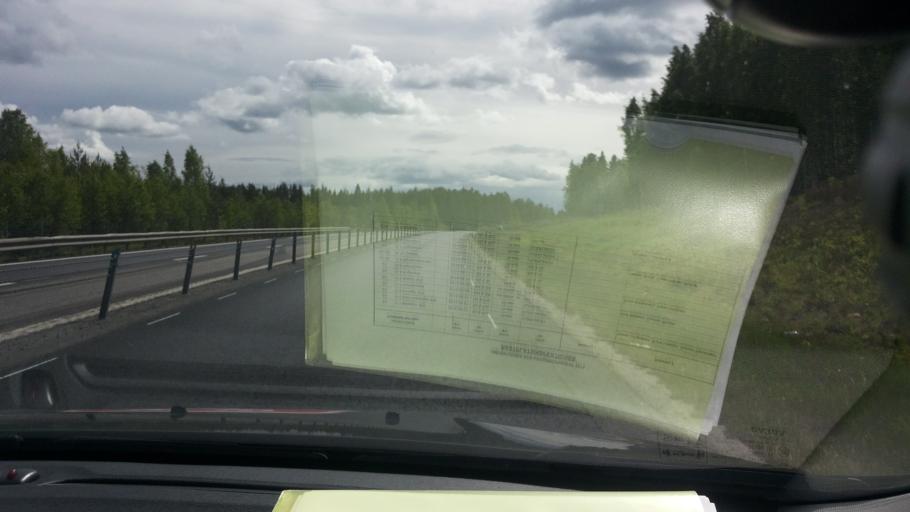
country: SE
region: Vaesternorrland
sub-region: Sundsvalls Kommun
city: Njurundabommen
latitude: 62.1974
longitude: 17.3704
